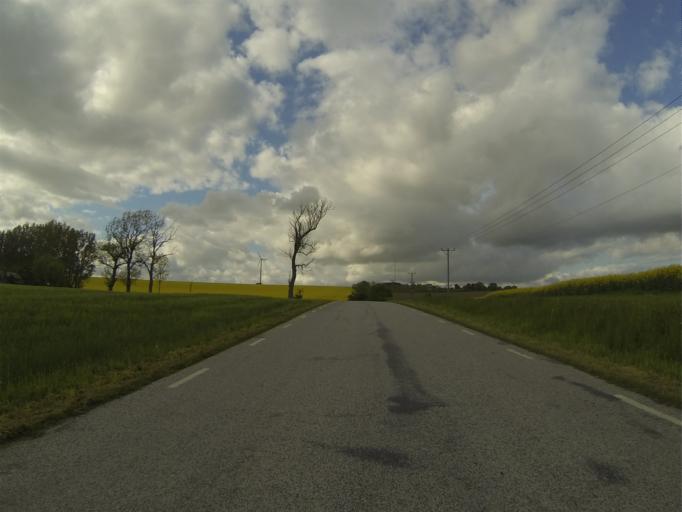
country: SE
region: Skane
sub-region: Staffanstorps Kommun
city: Staffanstorp
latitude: 55.6908
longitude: 13.2873
